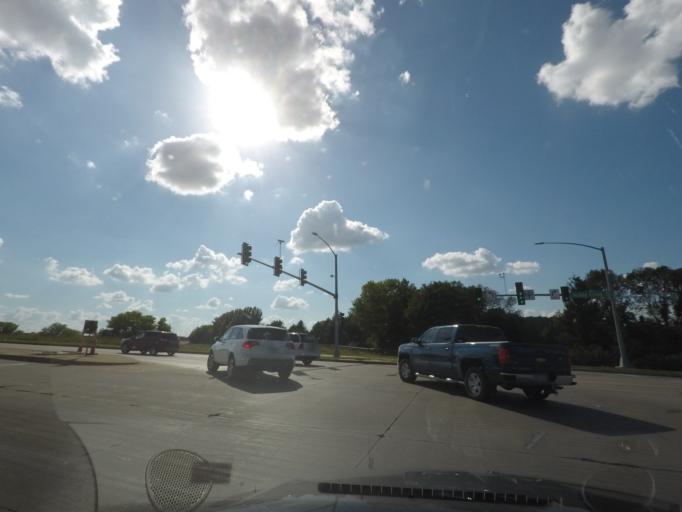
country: US
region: Iowa
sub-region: Dallas County
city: Waukee
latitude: 41.5933
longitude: -93.8089
